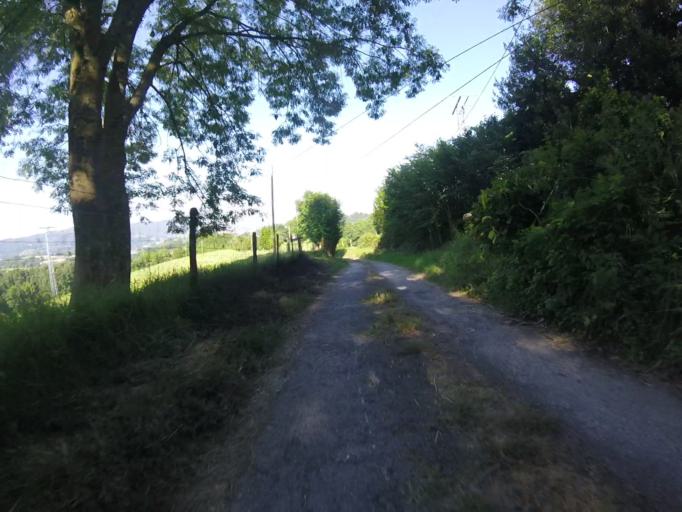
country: ES
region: Basque Country
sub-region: Provincia de Guipuzcoa
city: Pasaia
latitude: 43.3033
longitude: -1.9331
